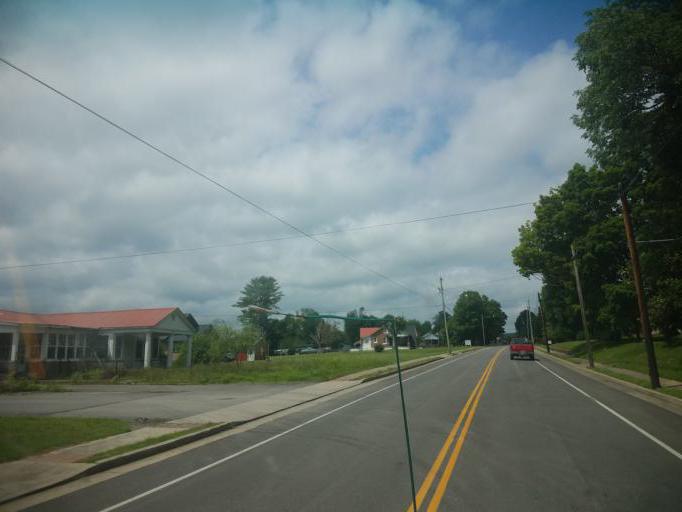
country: US
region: Kentucky
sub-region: Cumberland County
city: Burkesville
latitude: 36.8295
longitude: -85.5004
